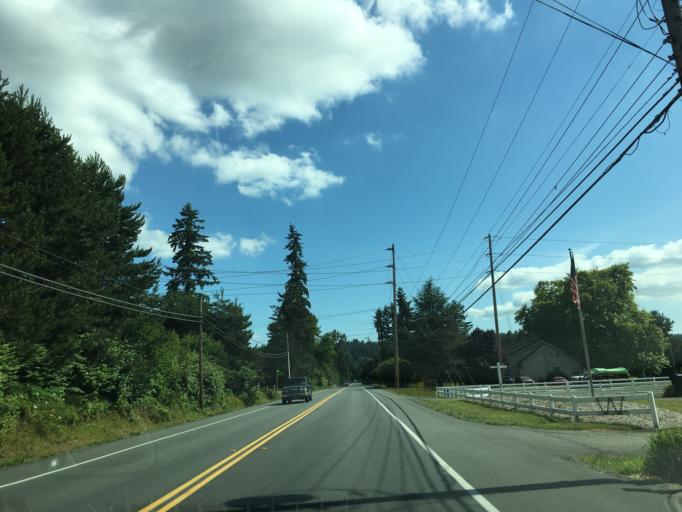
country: US
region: Washington
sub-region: King County
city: Kenmore
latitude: 47.7631
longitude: -122.2335
